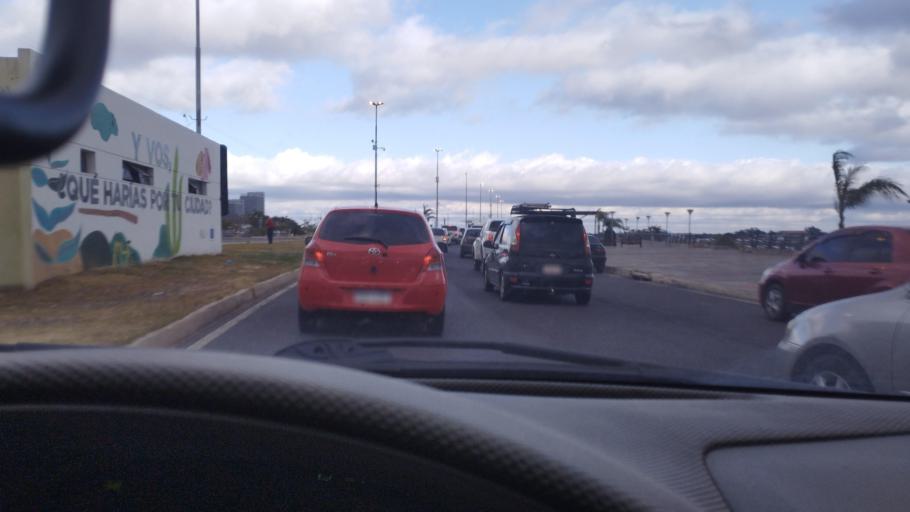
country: PY
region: Asuncion
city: Asuncion
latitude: -25.2790
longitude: -57.6333
